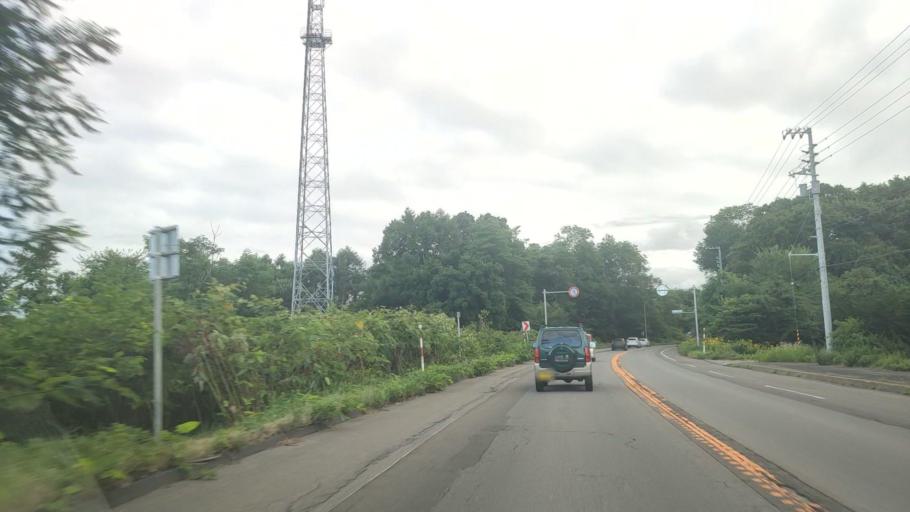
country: JP
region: Hokkaido
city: Nanae
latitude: 42.0666
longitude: 140.6032
